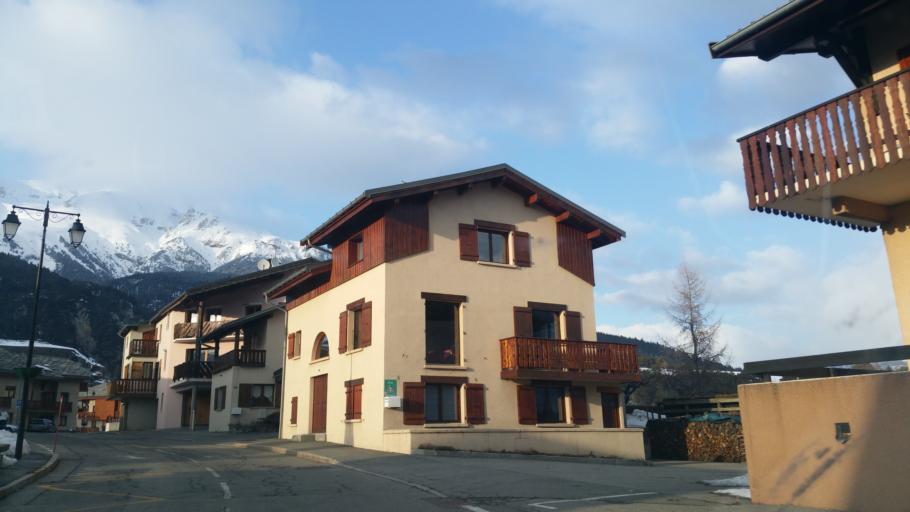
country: FR
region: Rhone-Alpes
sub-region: Departement de la Savoie
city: Modane
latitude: 45.2274
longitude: 6.7448
